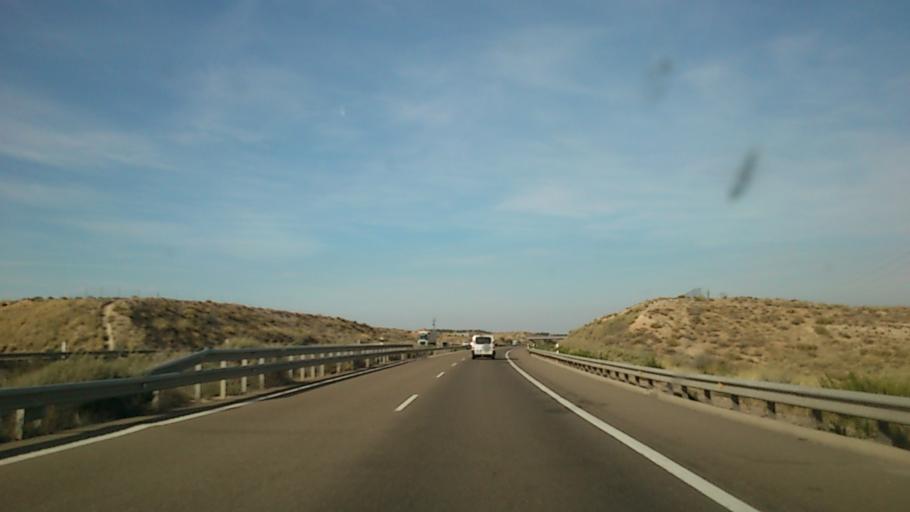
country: ES
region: Aragon
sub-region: Provincia de Zaragoza
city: Maria de Huerva
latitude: 41.5410
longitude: -1.0046
